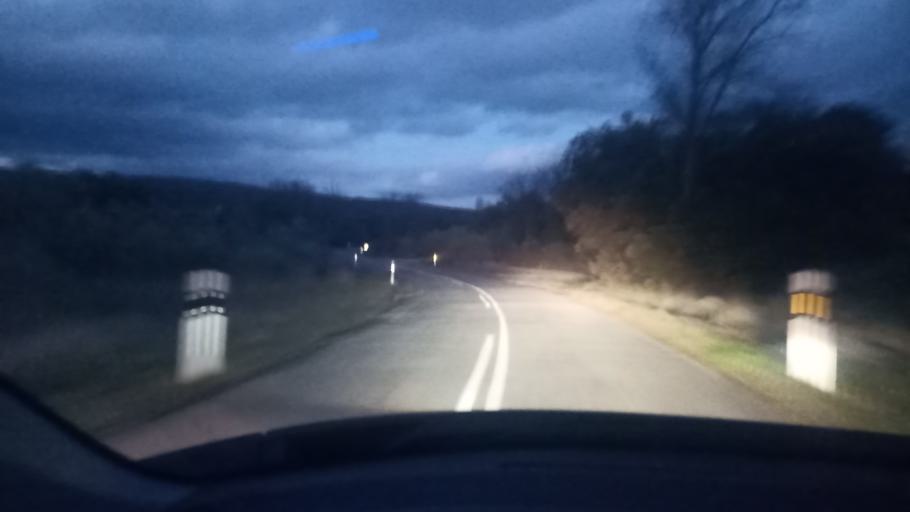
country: ES
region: Madrid
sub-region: Provincia de Madrid
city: Colmenar del Arroyo
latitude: 40.4296
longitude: -4.2171
